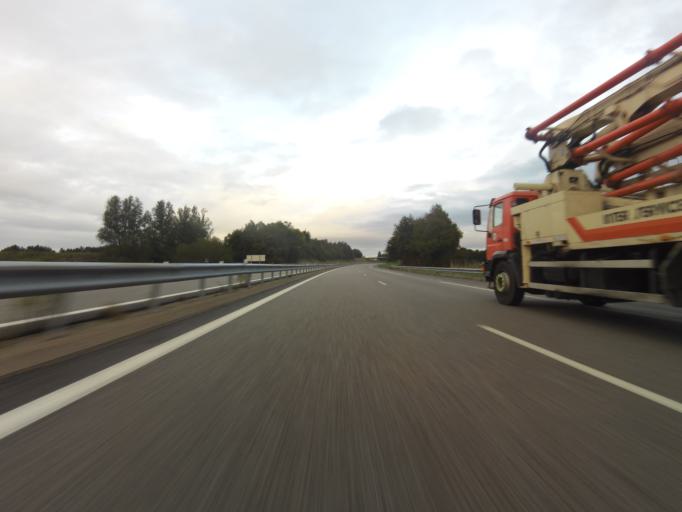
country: FR
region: Haute-Normandie
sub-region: Departement de la Seine-Maritime
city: Etainhus
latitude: 49.5650
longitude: 0.3426
